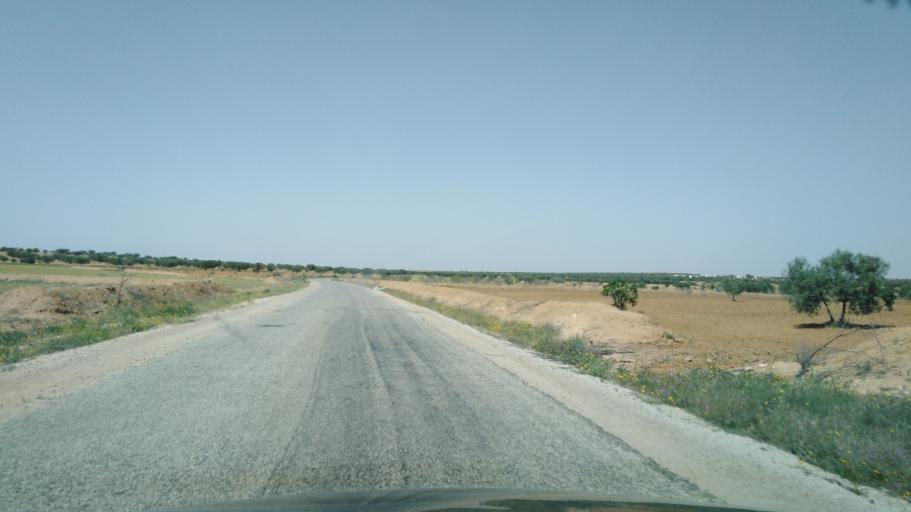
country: TN
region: Safaqis
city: Bi'r `Ali Bin Khalifah
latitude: 34.6791
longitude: 10.4069
